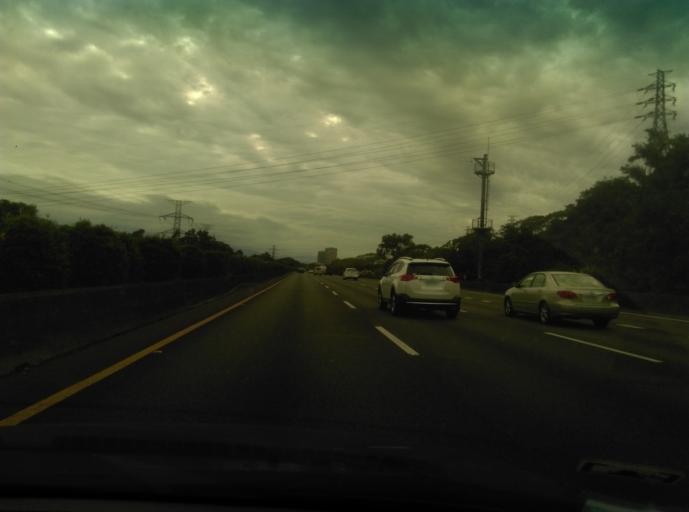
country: TW
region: Taiwan
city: Daxi
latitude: 24.9165
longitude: 121.2951
